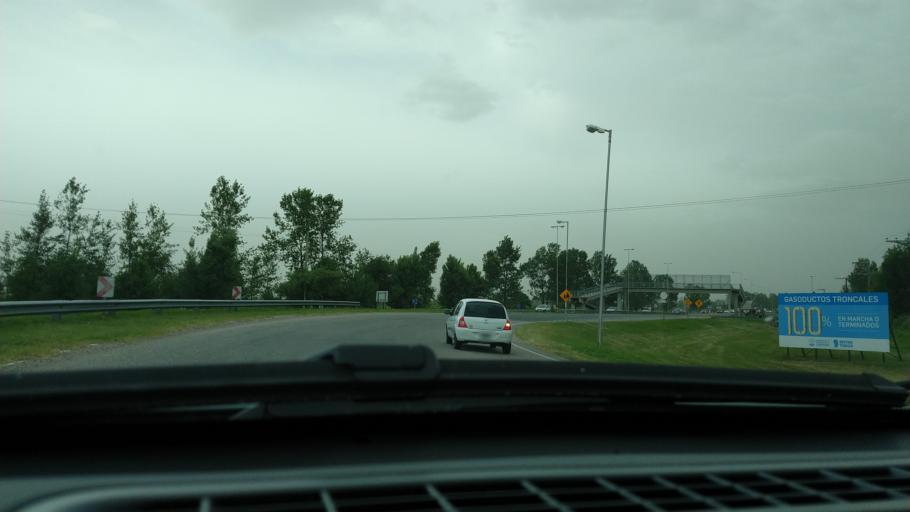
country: AR
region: Cordoba
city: Villa Allende
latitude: -31.3036
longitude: -64.2246
